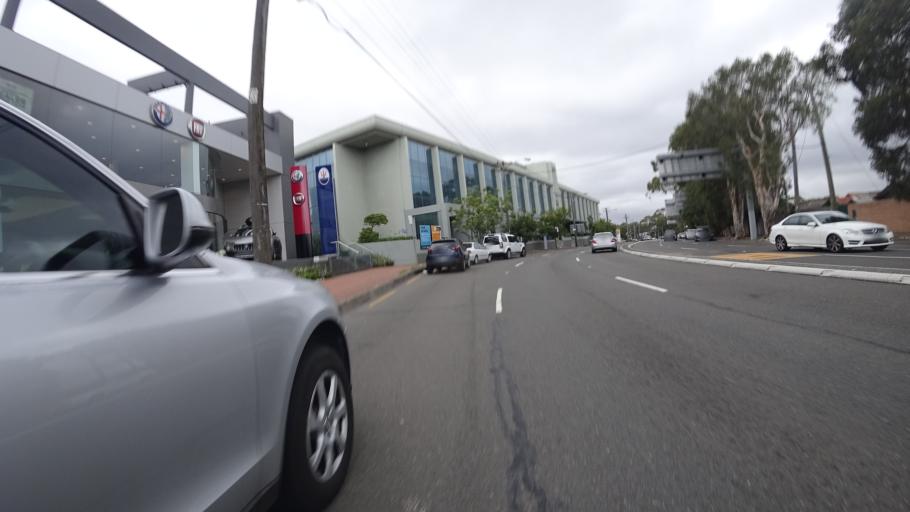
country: AU
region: New South Wales
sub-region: Willoughby
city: Artarmon
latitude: -33.8143
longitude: 151.1777
